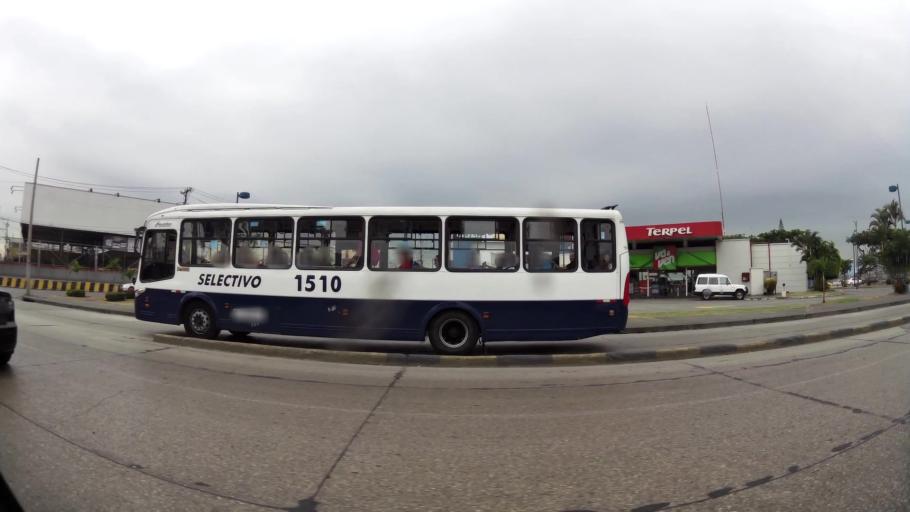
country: EC
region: Guayas
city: Eloy Alfaro
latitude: -2.1630
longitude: -79.8921
